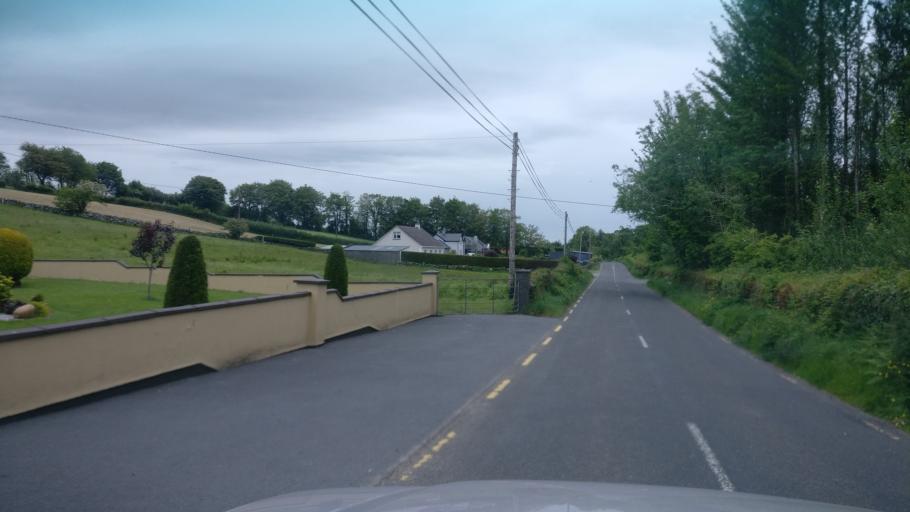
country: IE
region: Connaught
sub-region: County Galway
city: Loughrea
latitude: 53.0896
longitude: -8.4736
